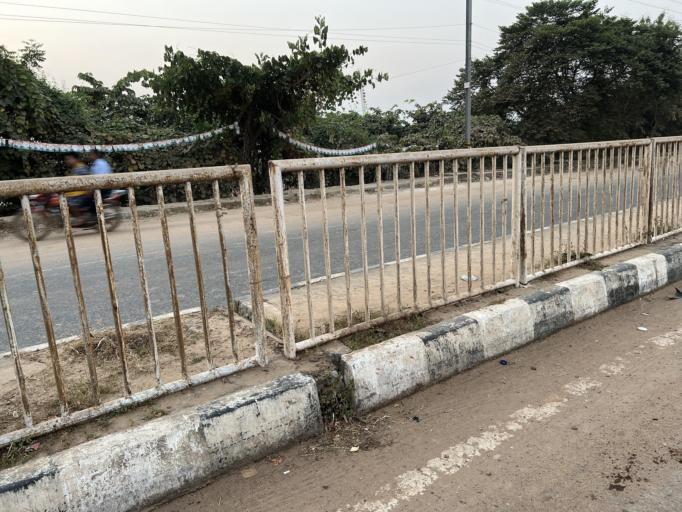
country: IN
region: Odisha
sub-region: Khordha
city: Bhubaneshwar
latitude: 20.3586
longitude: 85.8892
